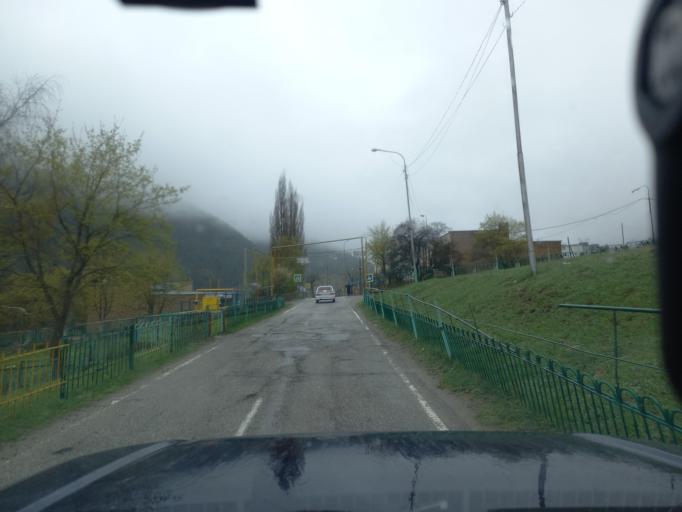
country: RU
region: Kabardino-Balkariya
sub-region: El'brusskiy Rayon
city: El'brus
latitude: 43.2778
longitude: 42.6885
